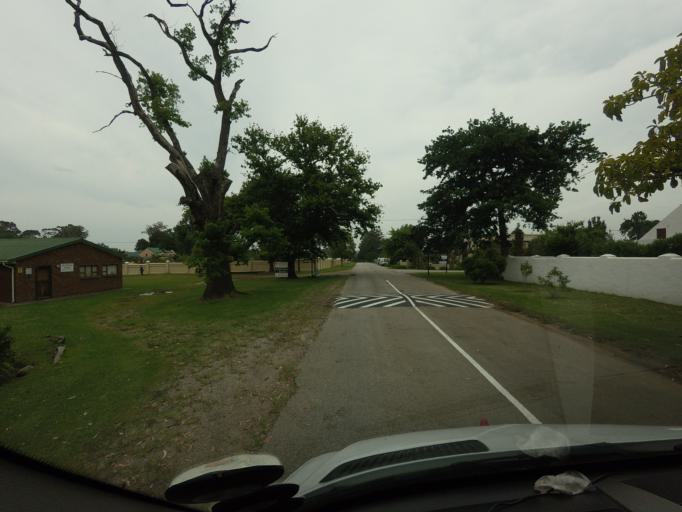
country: ZA
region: Eastern Cape
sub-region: Cacadu District Municipality
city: Kareedouw
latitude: -33.9716
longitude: 23.8870
